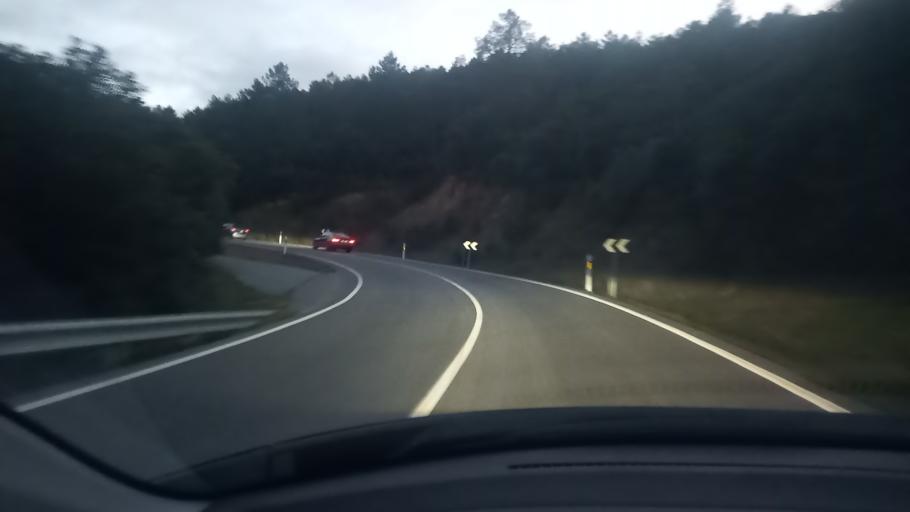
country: ES
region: Madrid
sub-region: Provincia de Madrid
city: Robledo de Chavela
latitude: 40.4575
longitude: -4.2641
